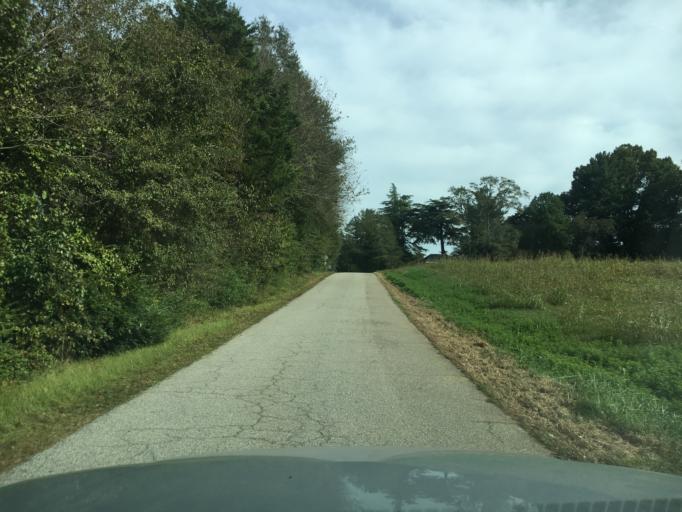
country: US
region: South Carolina
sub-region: Spartanburg County
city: Duncan
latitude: 34.9173
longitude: -82.1462
